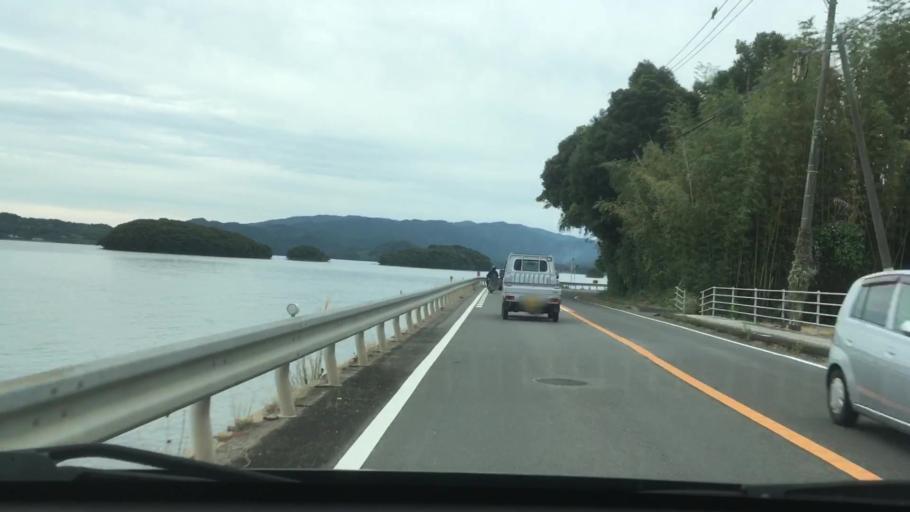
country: JP
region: Nagasaki
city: Sasebo
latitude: 33.0300
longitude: 129.7434
